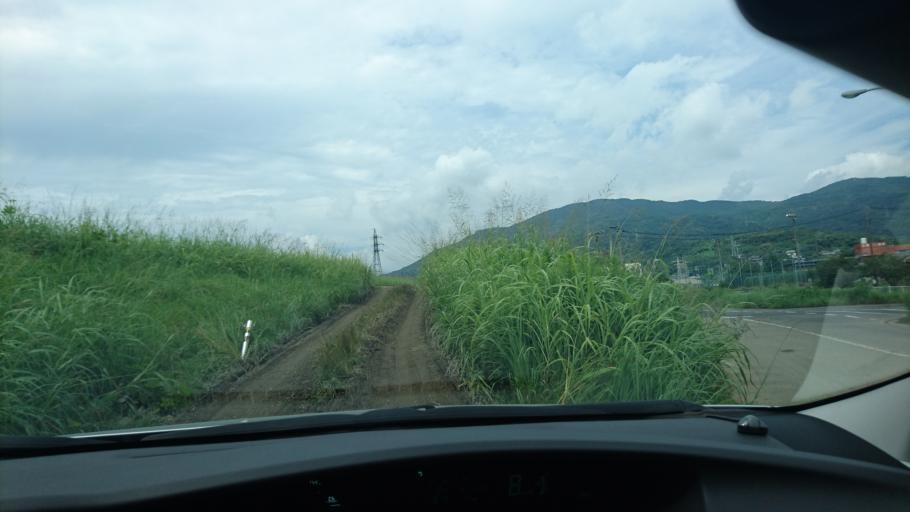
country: JP
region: Saga Prefecture
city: Takeocho-takeo
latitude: 33.2099
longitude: 130.1117
